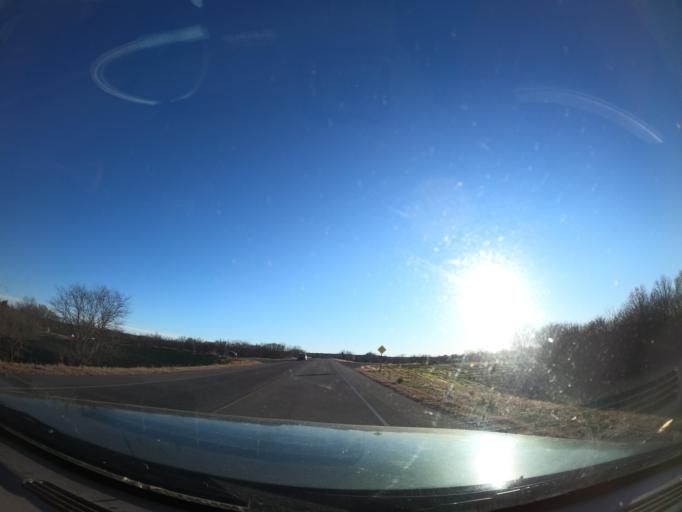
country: US
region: Oklahoma
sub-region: Pittsburg County
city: Hartshorne
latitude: 34.8488
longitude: -95.5368
